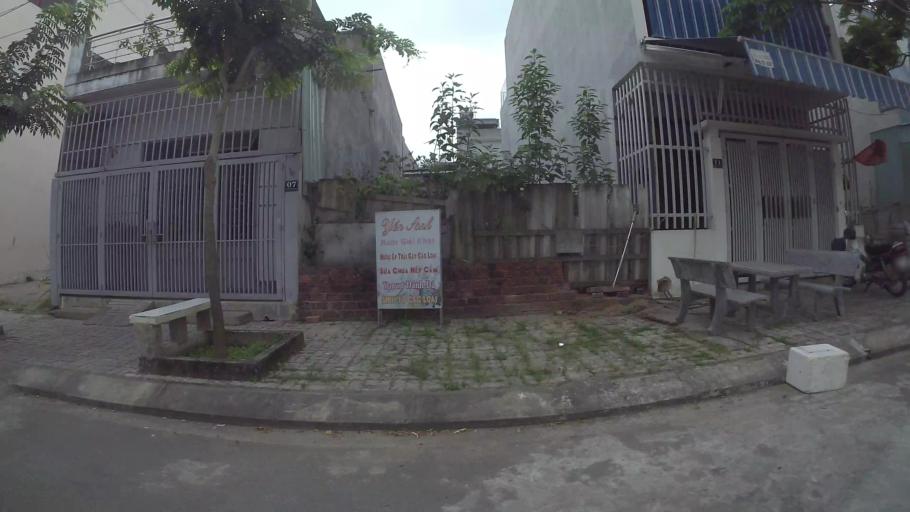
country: VN
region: Da Nang
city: Cam Le
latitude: 16.0354
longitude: 108.1750
